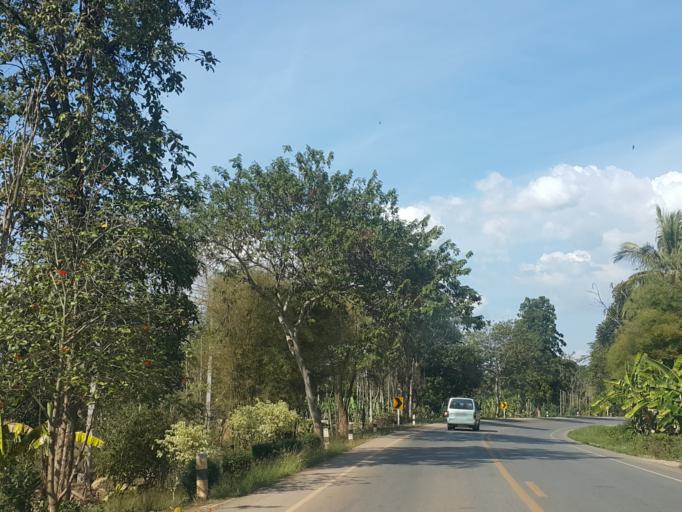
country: TH
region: Sukhothai
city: Sawankhalok
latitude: 17.2750
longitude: 99.8298
